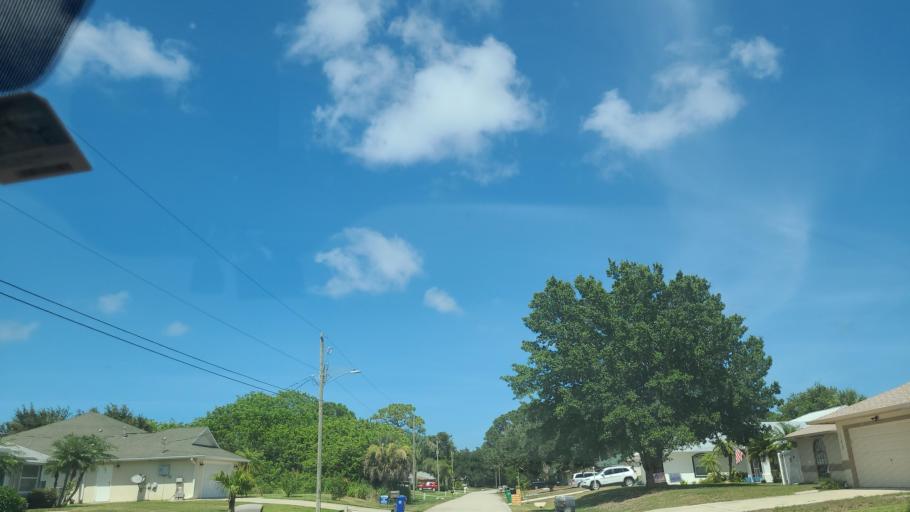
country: US
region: Florida
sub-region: Indian River County
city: Sebastian
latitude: 27.7660
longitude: -80.4727
